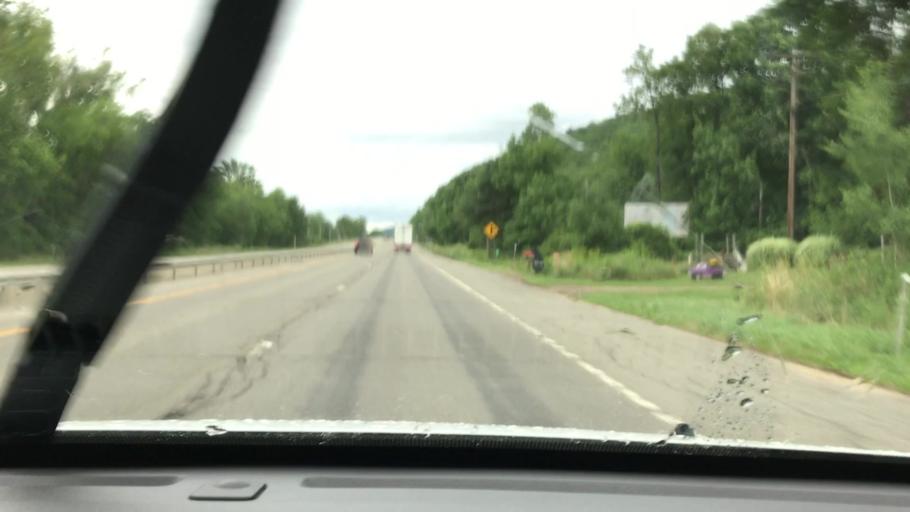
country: US
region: Pennsylvania
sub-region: McKean County
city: Foster Brook
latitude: 42.0500
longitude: -78.6349
